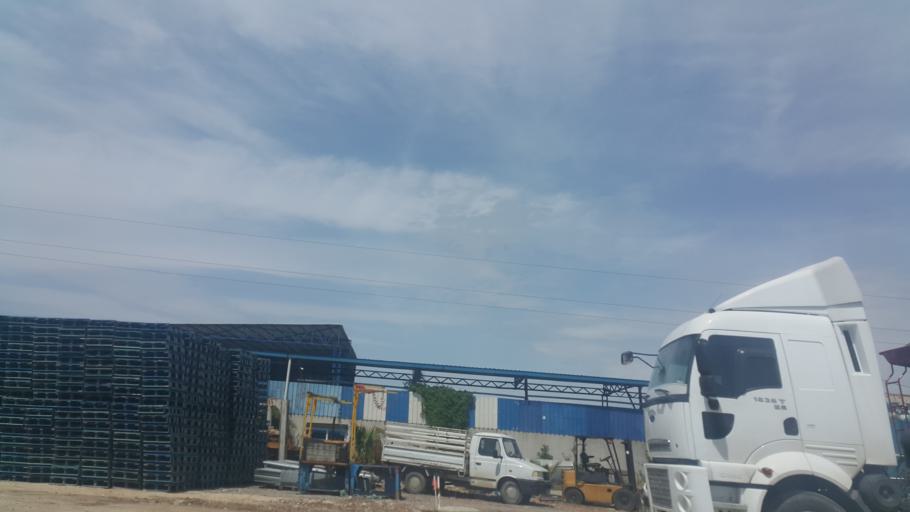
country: TR
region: Adana
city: Yuregir
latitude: 36.9781
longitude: 35.4677
